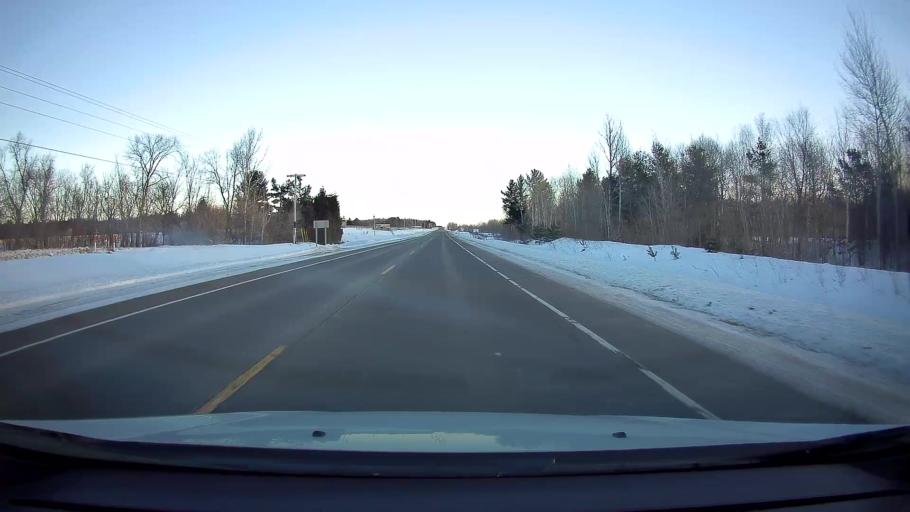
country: US
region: Wisconsin
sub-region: Barron County
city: Cumberland
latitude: 45.6122
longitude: -92.0090
